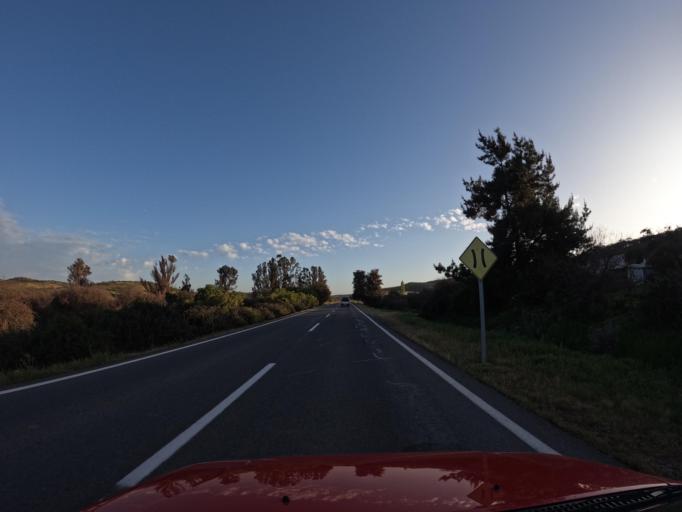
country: CL
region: O'Higgins
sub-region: Provincia de Colchagua
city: Santa Cruz
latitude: -34.2902
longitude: -71.7301
